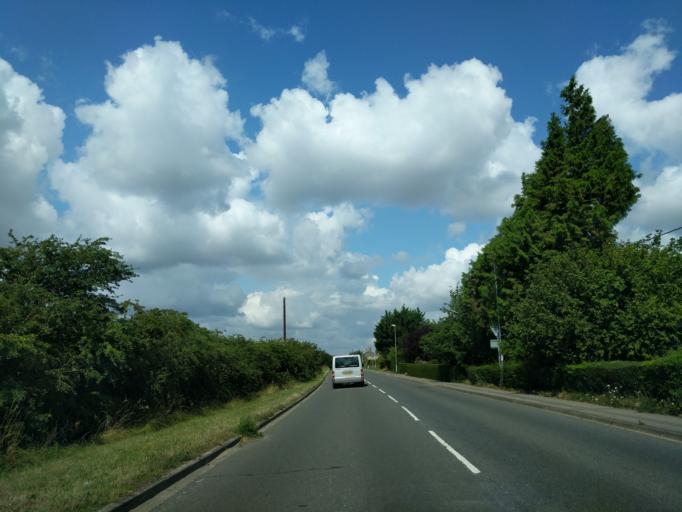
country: GB
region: England
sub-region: Cambridgeshire
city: Isleham
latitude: 52.3120
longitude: 0.3795
